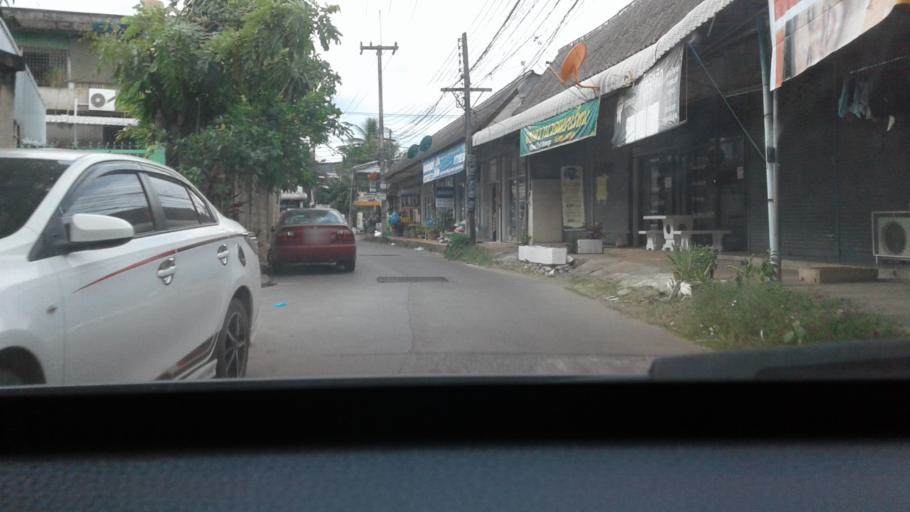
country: TH
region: Changwat Udon Thani
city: Udon Thani
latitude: 17.4096
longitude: 102.8006
